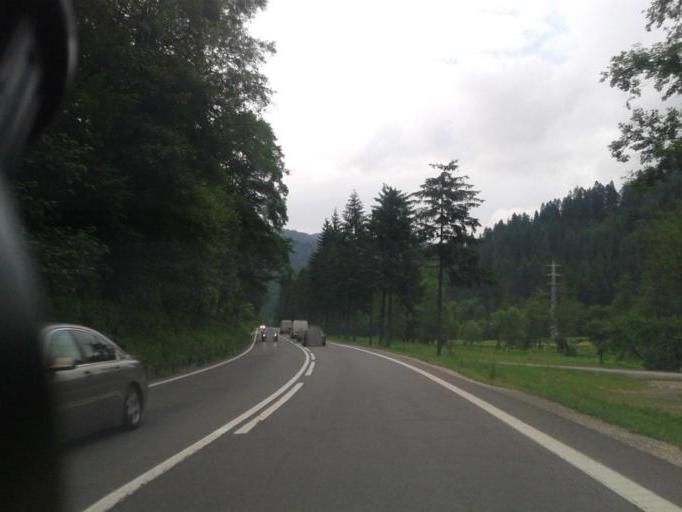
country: RO
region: Brasov
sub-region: Oras Predeal
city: Predeal
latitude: 45.5427
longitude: 25.5885
